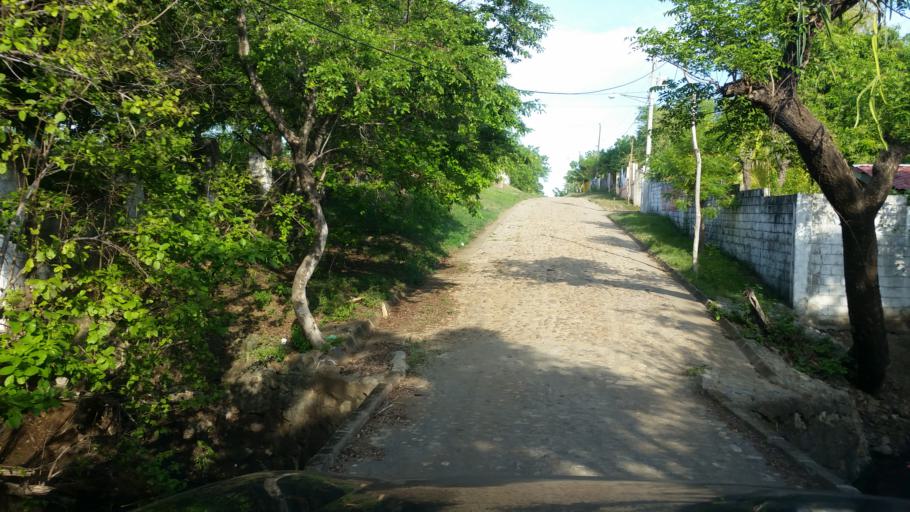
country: NI
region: Managua
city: Masachapa
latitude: 11.7579
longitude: -86.4902
